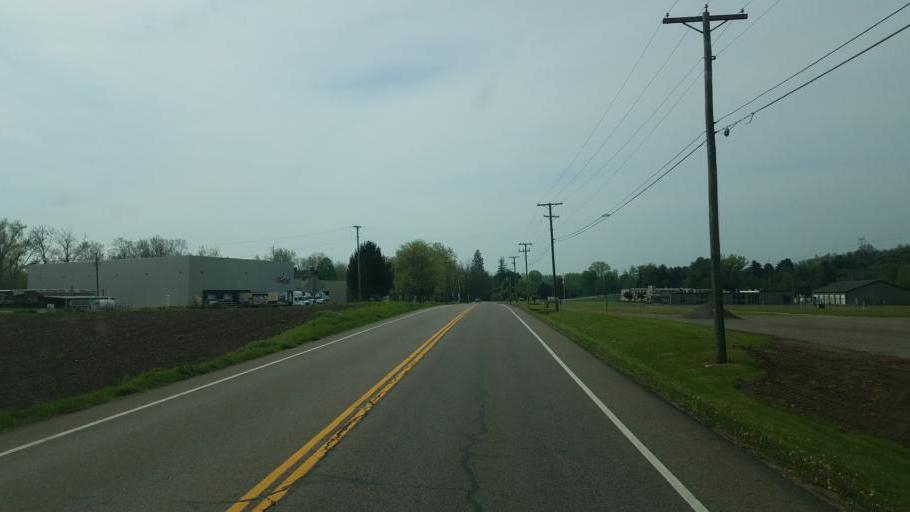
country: US
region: Ohio
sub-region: Licking County
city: Utica
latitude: 40.2172
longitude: -82.4433
